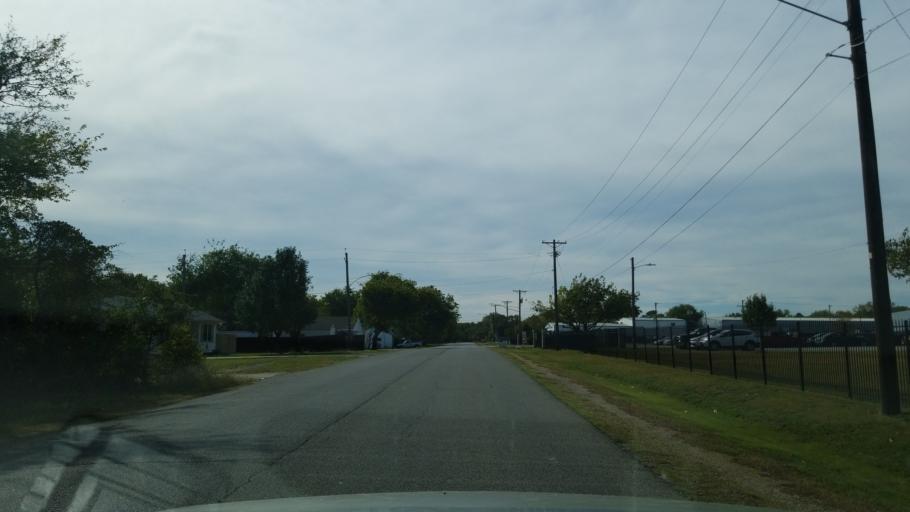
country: US
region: Texas
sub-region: Dallas County
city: Garland
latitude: 32.9082
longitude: -96.6530
